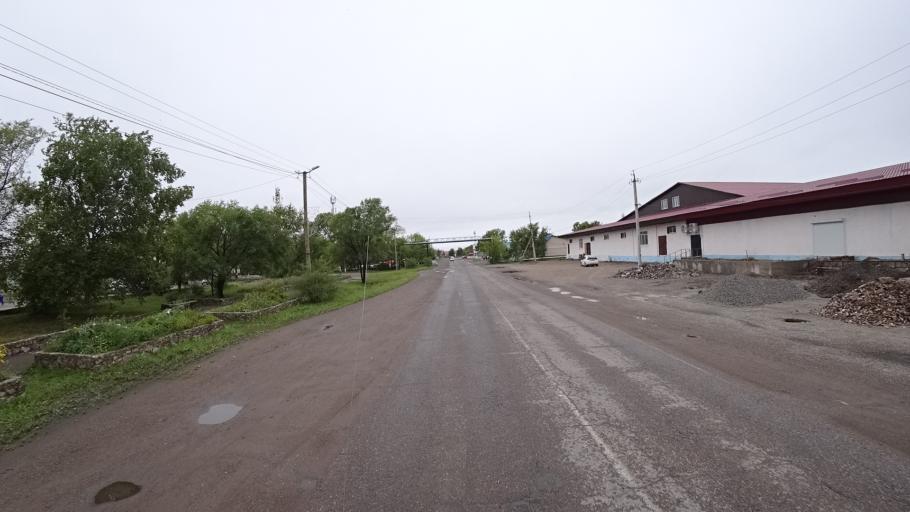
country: RU
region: Primorskiy
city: Monastyrishche
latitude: 44.2047
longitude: 132.4452
